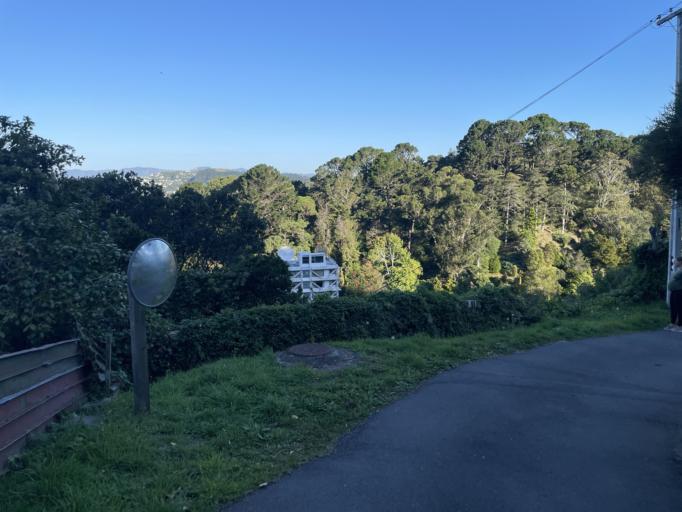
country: NZ
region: Wellington
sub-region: Wellington City
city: Kelburn
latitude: -41.2793
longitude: 174.7666
